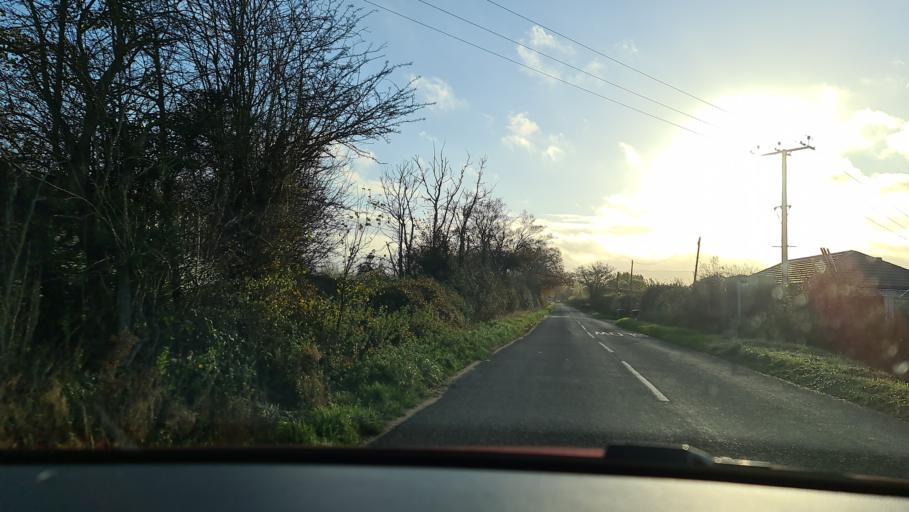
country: GB
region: England
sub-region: Buckinghamshire
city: Aylesbury
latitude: 51.7802
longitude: -0.8127
